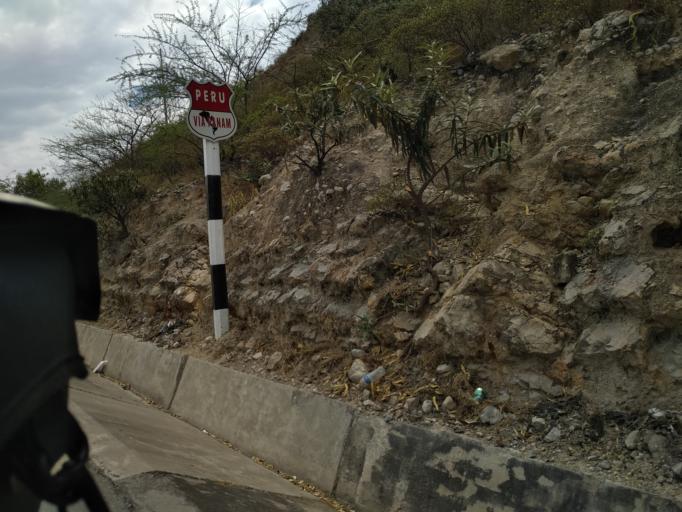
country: PE
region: Cajamarca
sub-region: Provincia de Jaen
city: Bellavista
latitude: -5.7520
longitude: -78.6893
